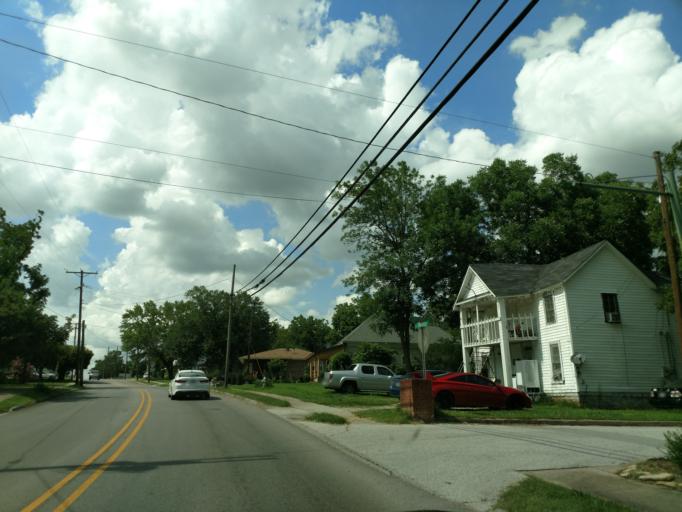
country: US
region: Arkansas
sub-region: Carroll County
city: Berryville
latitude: 36.3625
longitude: -93.5645
